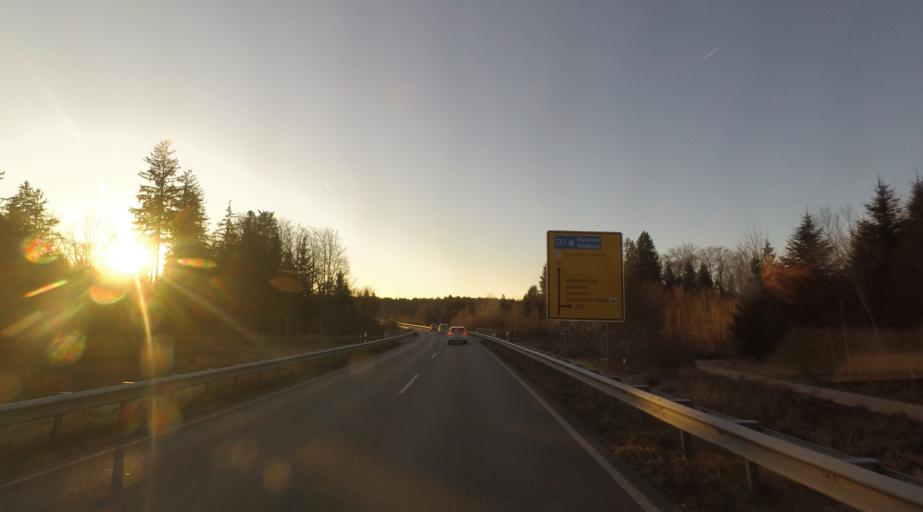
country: DE
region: Bavaria
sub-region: Upper Bavaria
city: Traunstein
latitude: 47.8810
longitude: 12.6634
